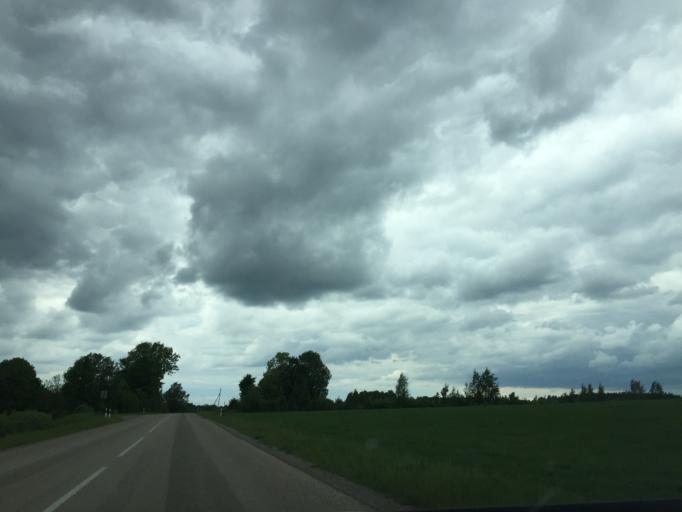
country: LV
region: Dagda
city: Dagda
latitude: 56.1235
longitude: 27.4696
